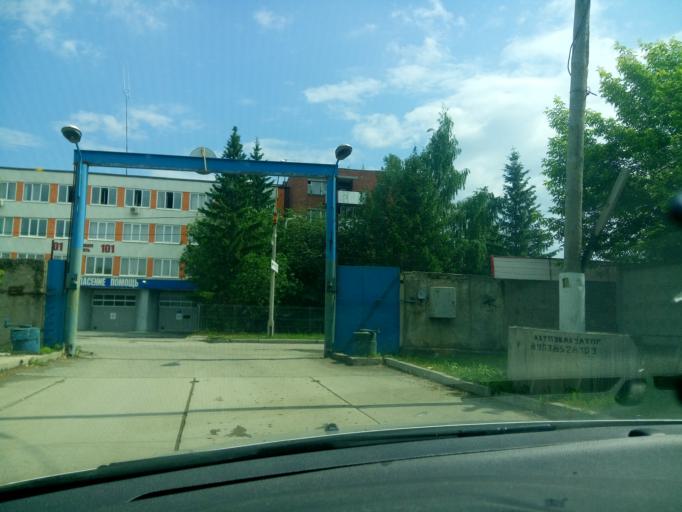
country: RU
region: Sverdlovsk
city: Yekaterinburg
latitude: 56.8580
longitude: 60.6632
